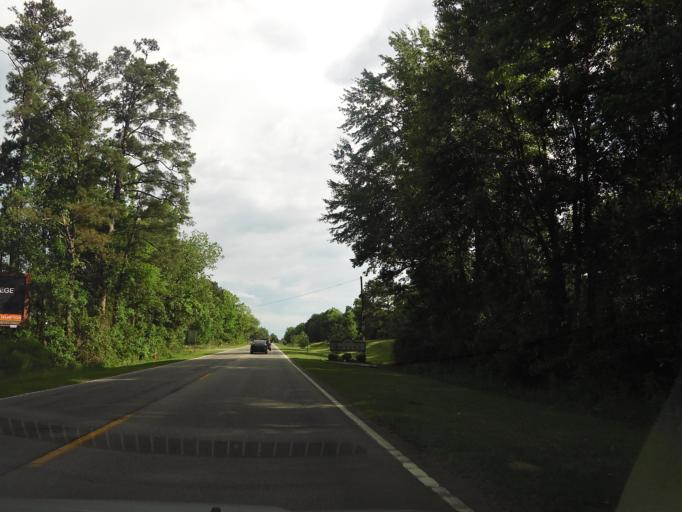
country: US
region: South Carolina
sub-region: Hampton County
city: Estill
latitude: 32.7687
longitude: -81.2410
